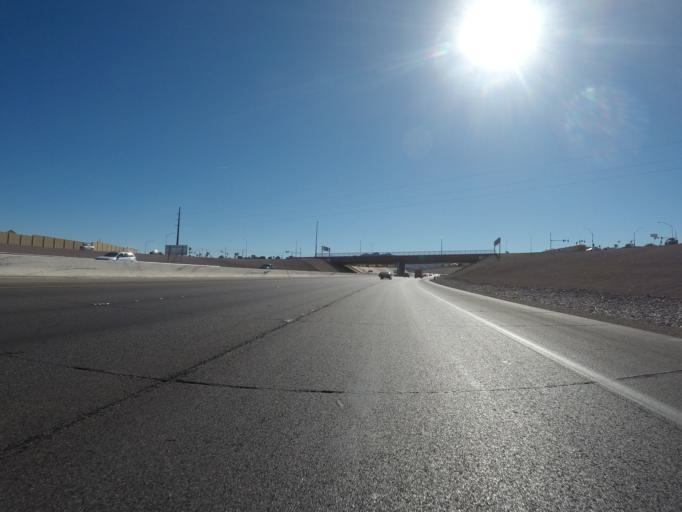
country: US
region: Nevada
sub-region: Clark County
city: Henderson
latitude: 36.0134
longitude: -114.9912
